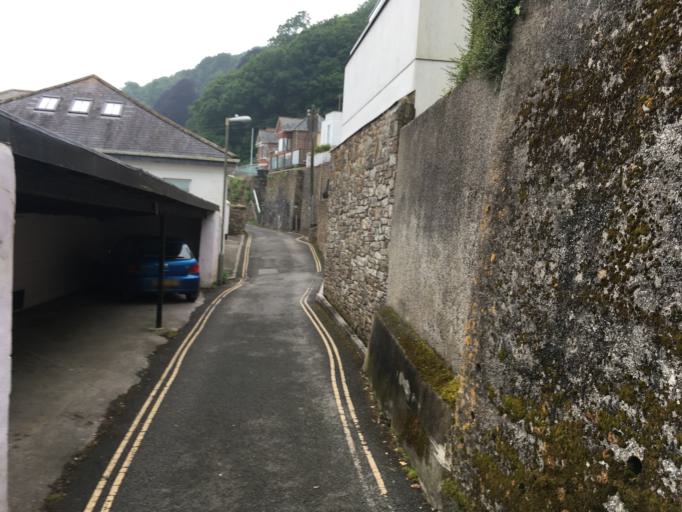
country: GB
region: England
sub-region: Devon
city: Dartmouth
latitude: 50.3467
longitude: -3.5783
